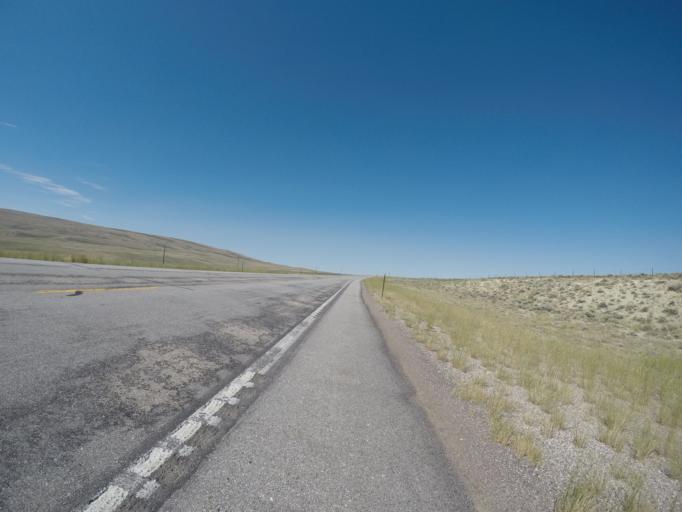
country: US
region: Wyoming
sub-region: Carbon County
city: Saratoga
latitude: 41.7970
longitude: -106.7196
